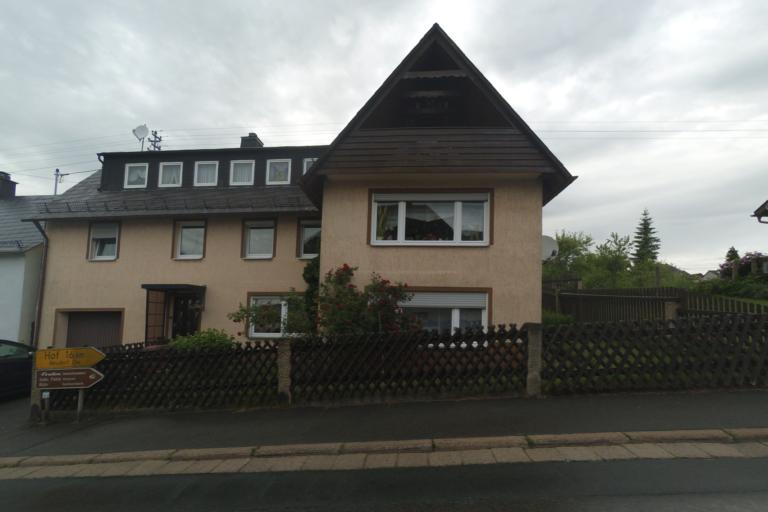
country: DE
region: Bavaria
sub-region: Upper Franconia
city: Schauenstein
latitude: 50.2786
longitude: 11.7446
